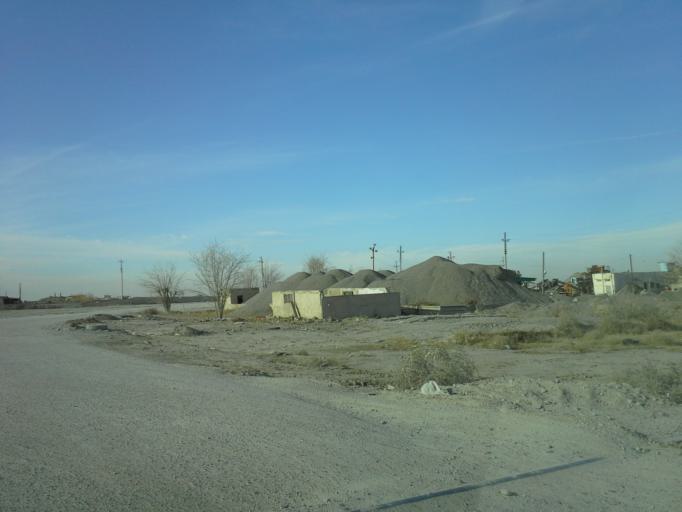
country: TM
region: Ahal
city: Abadan
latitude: 38.0279
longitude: 58.1638
